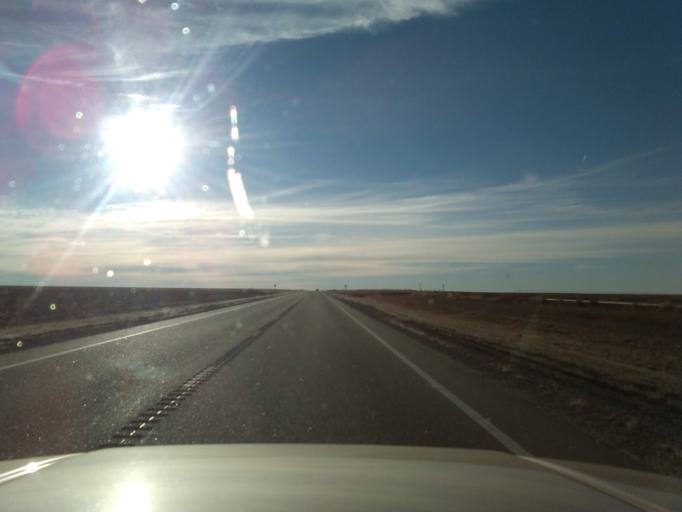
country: US
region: Kansas
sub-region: Sheridan County
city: Hoxie
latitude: 39.5277
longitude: -100.6059
